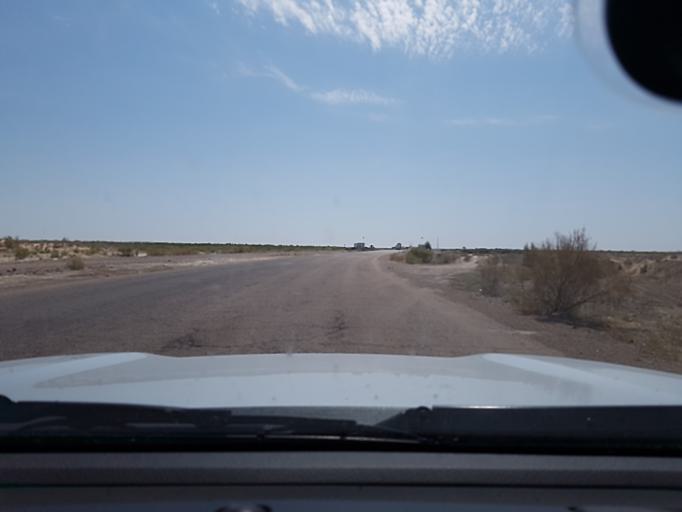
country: TM
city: Akdepe
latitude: 41.4547
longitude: 58.5577
